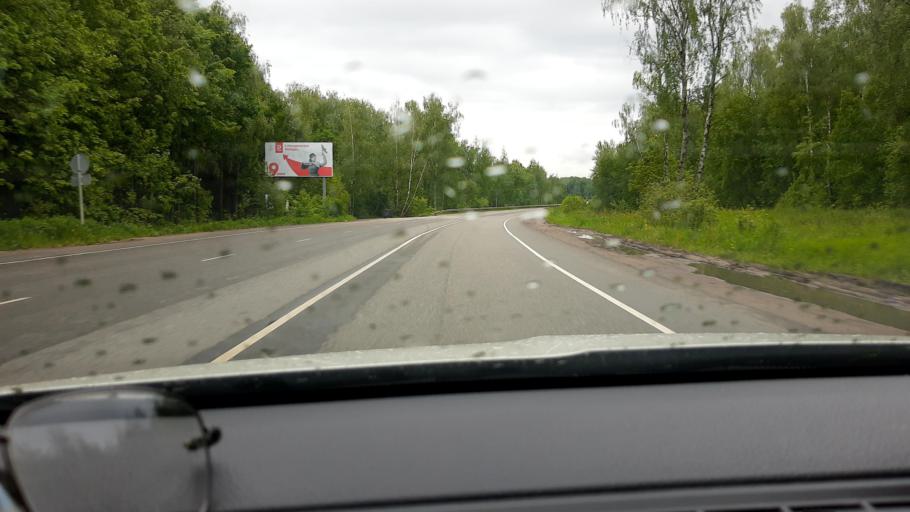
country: RU
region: Moskovskaya
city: Petrovskaya
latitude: 55.5288
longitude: 37.7853
